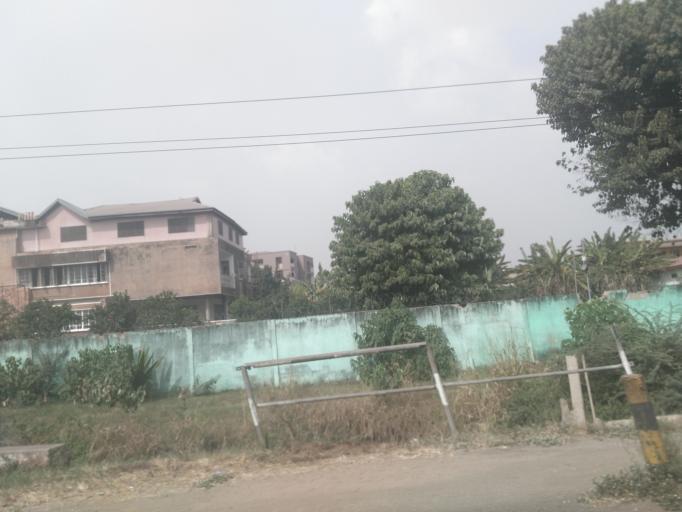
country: GH
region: Ashanti
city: Kumasi
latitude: 6.6877
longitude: -1.5827
